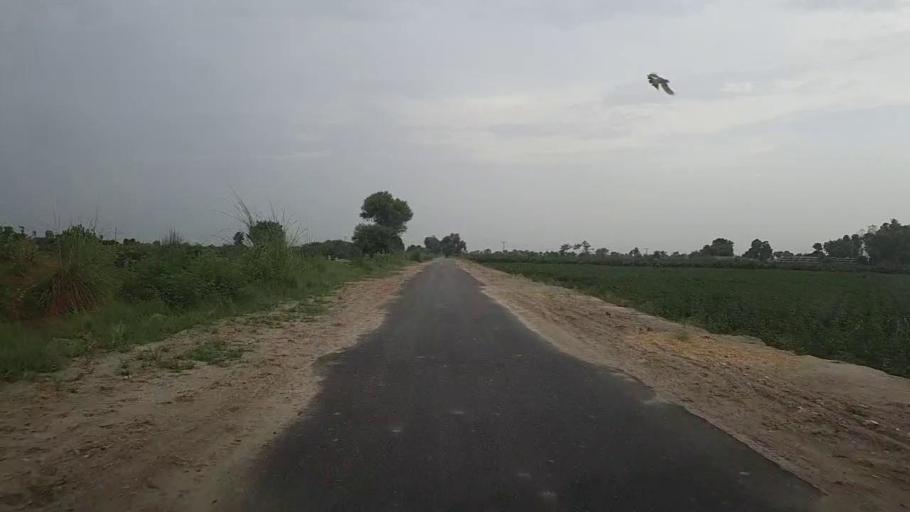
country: PK
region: Sindh
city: Karaundi
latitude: 26.9858
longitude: 68.3546
